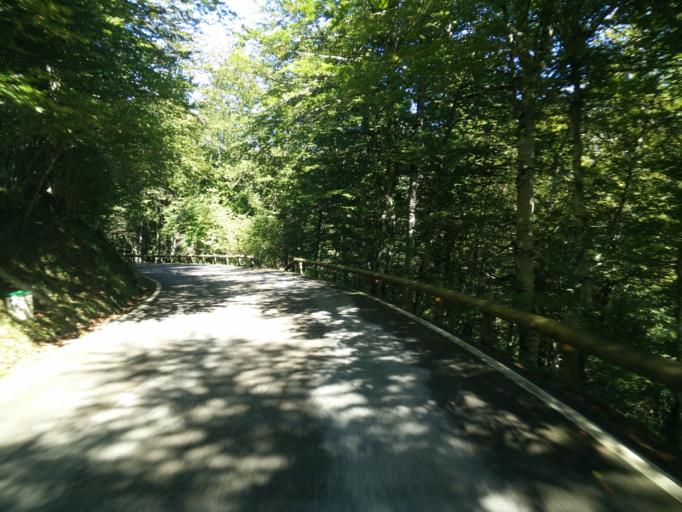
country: ES
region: Cantabria
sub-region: Provincia de Cantabria
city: Ruente
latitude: 43.1031
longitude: -4.2771
